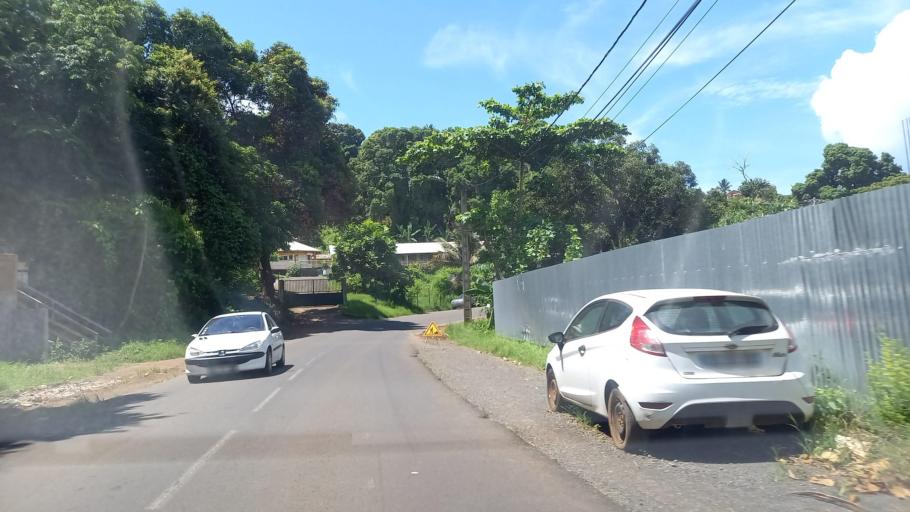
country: YT
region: Sada
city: Sada
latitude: -12.8549
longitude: 45.1034
